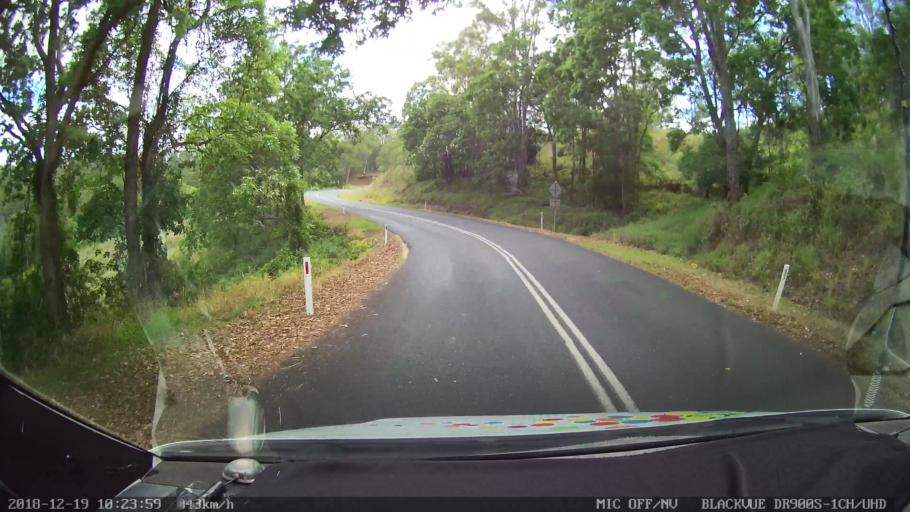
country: AU
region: New South Wales
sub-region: Lismore Municipality
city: Larnook
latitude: -28.5949
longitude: 153.0757
